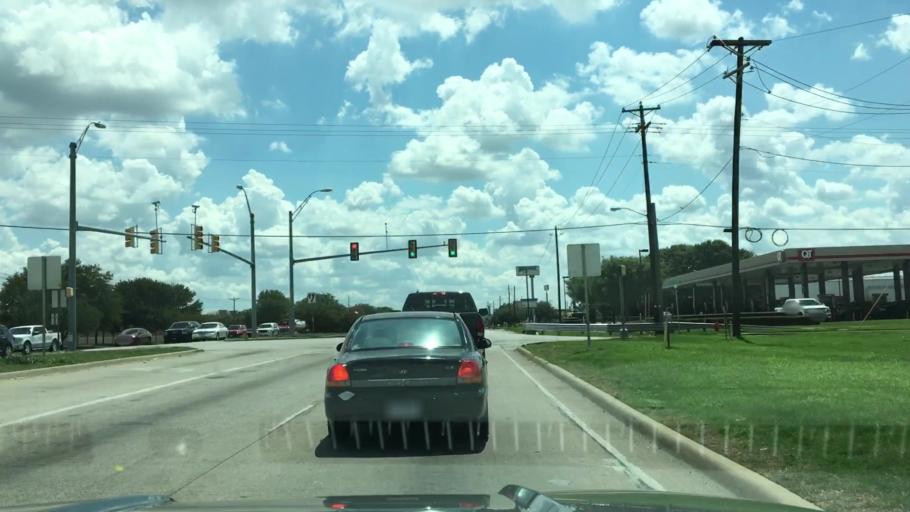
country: US
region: Texas
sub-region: Tarrant County
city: Blue Mound
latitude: 32.8483
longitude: -97.3431
